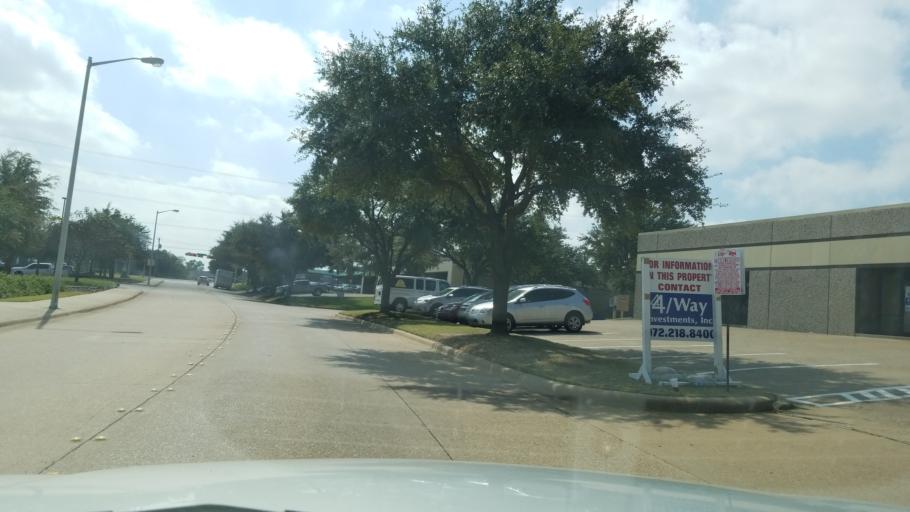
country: US
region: Texas
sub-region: Dallas County
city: Garland
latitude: 32.9106
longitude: -96.6566
